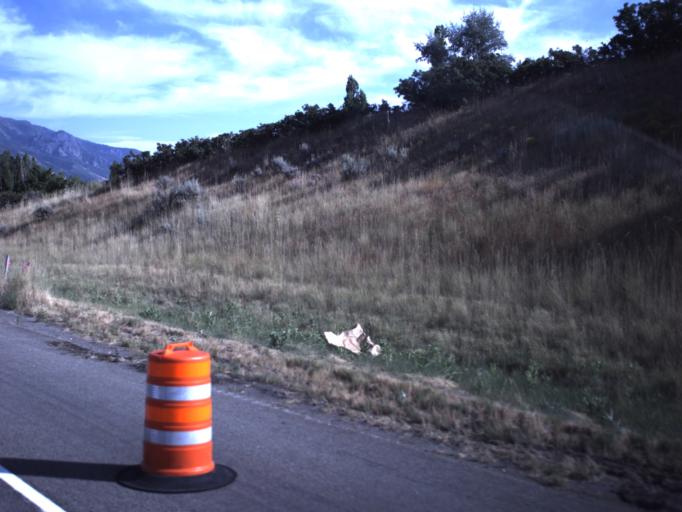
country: US
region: Utah
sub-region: Weber County
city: Washington Terrace
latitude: 41.1614
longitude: -111.9485
